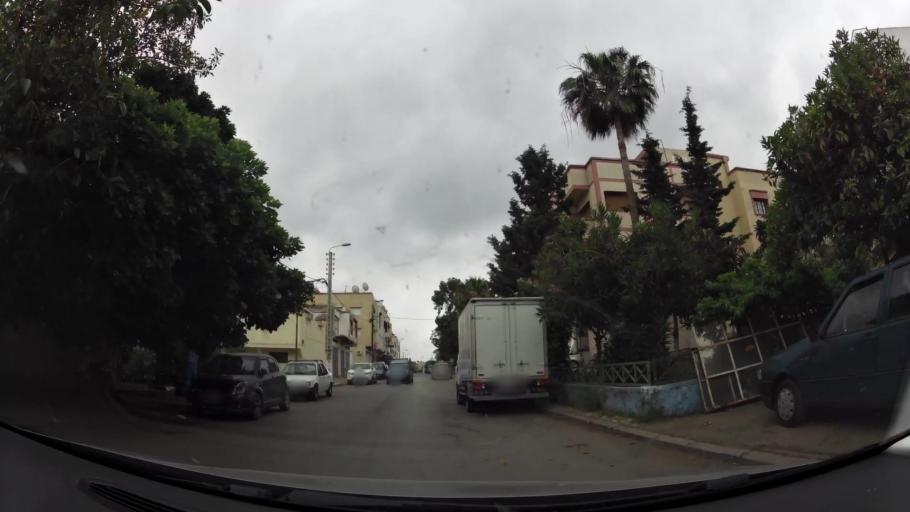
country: MA
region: Rabat-Sale-Zemmour-Zaer
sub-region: Rabat
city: Rabat
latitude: 33.9806
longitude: -6.8155
